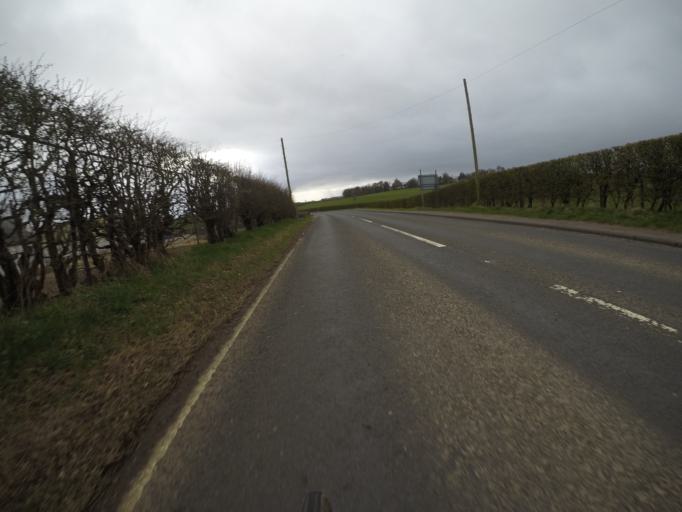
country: GB
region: Scotland
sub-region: East Ayrshire
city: Crosshouse
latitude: 55.6122
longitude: -4.5623
